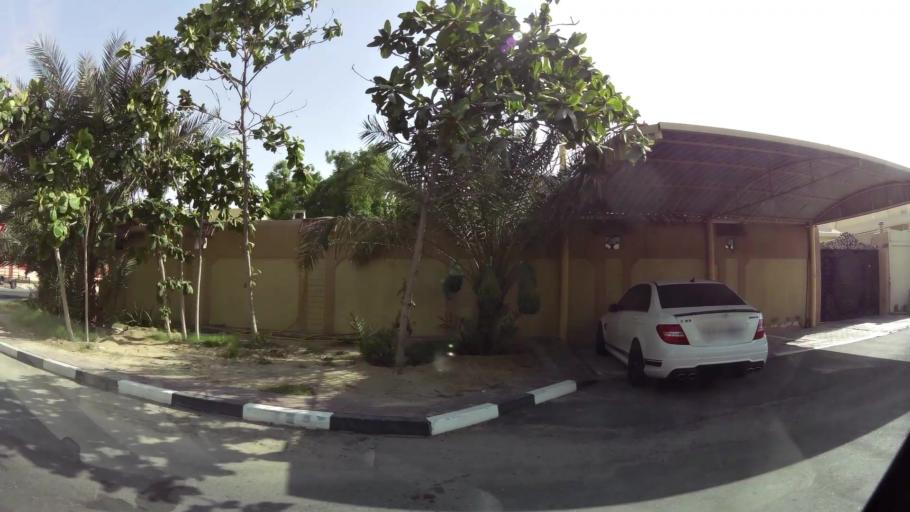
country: AE
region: Dubai
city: Dubai
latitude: 25.1738
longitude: 55.2492
